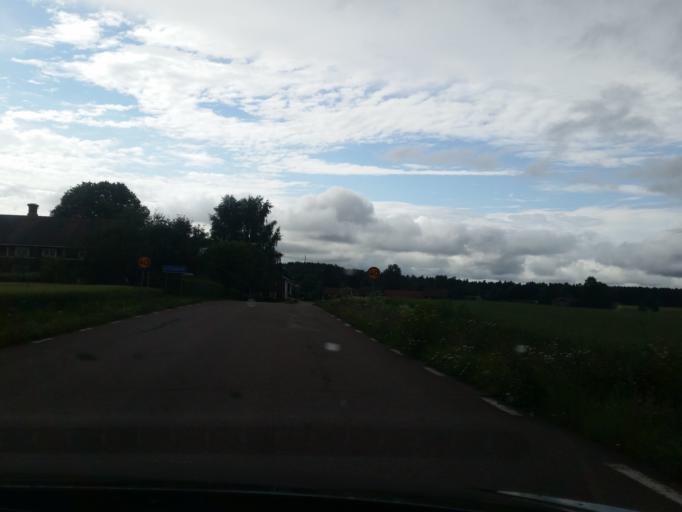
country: SE
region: Dalarna
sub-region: Leksand Municipality
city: Smedby
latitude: 60.7106
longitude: 15.0300
